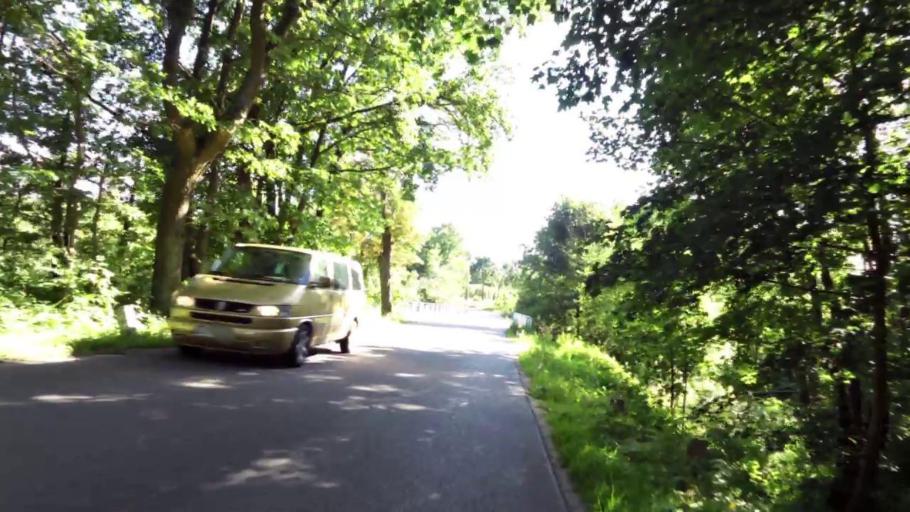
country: PL
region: West Pomeranian Voivodeship
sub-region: Powiat slawienski
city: Slawno
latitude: 54.4537
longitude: 16.7399
